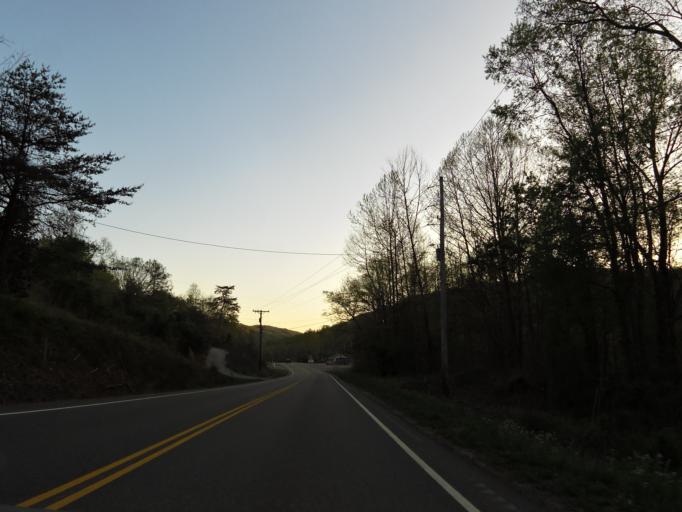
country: US
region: Tennessee
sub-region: Campbell County
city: Fincastle
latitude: 36.4305
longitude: -84.0817
